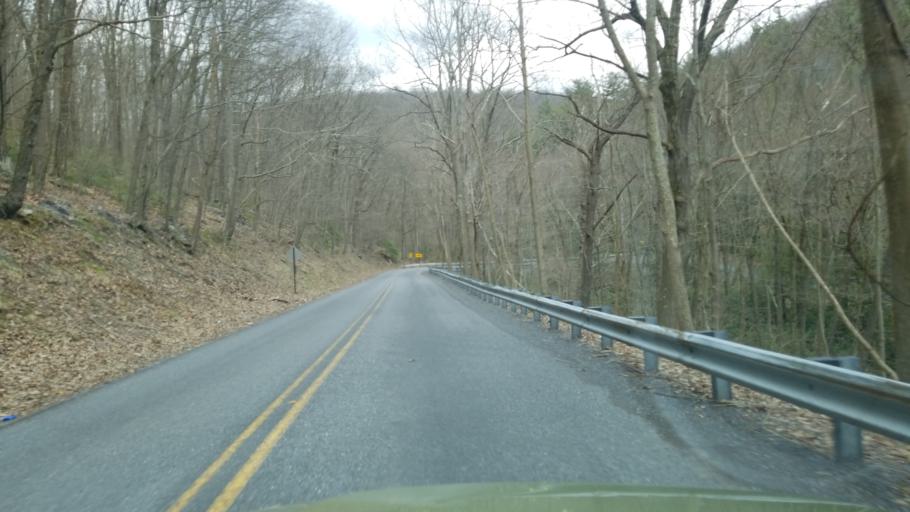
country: US
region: Pennsylvania
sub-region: Blair County
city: Tipton
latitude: 40.6919
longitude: -78.3314
